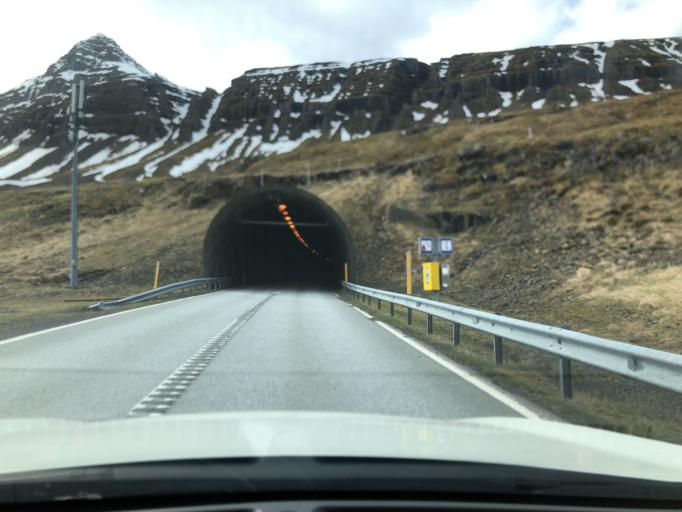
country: IS
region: East
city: Reydarfjoerdur
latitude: 65.0123
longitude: -14.1991
